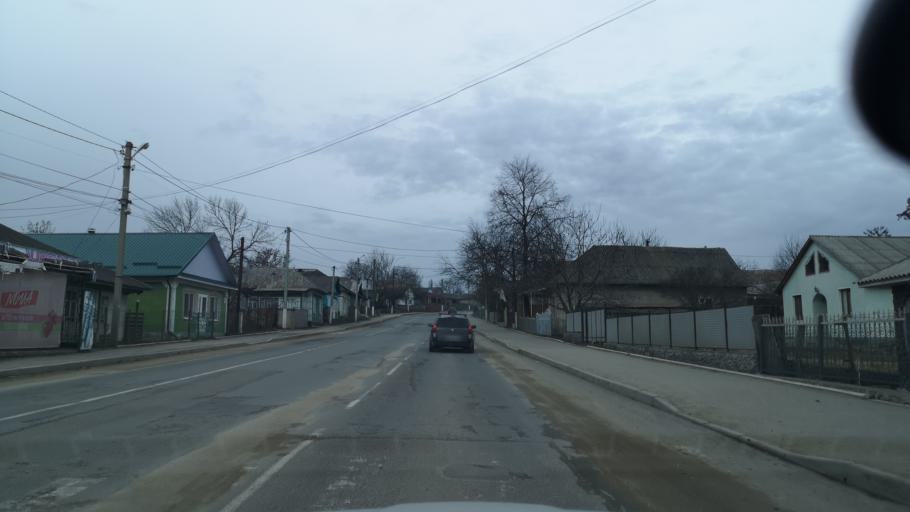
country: MD
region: Raionul Edinet
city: Edinet
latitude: 48.1645
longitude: 27.3140
